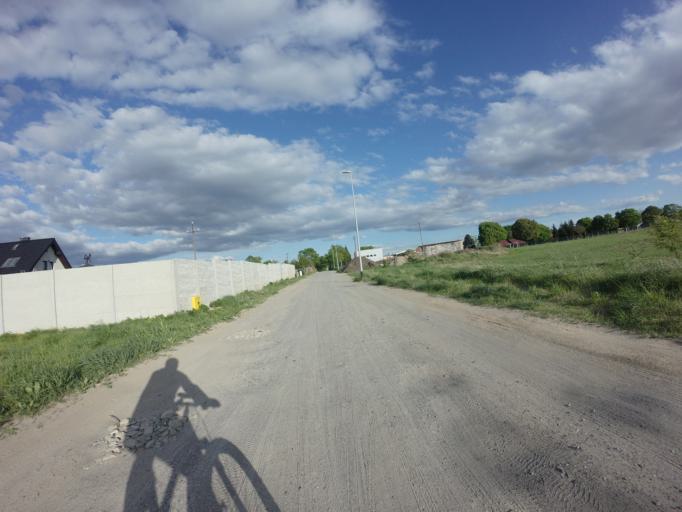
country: PL
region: West Pomeranian Voivodeship
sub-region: Powiat choszczenski
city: Choszczno
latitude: 53.1585
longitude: 15.3898
